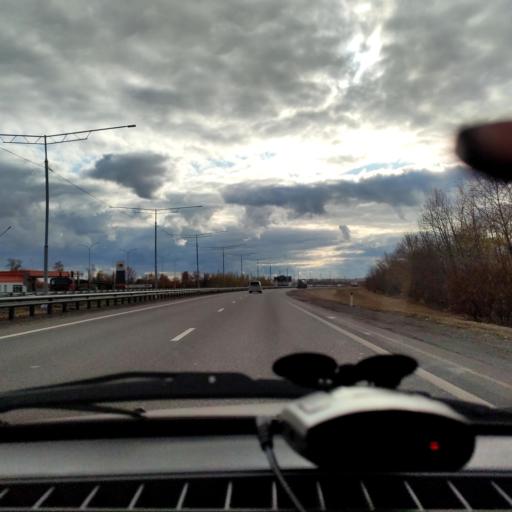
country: RU
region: Voronezj
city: Ramon'
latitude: 51.9931
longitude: 39.2190
